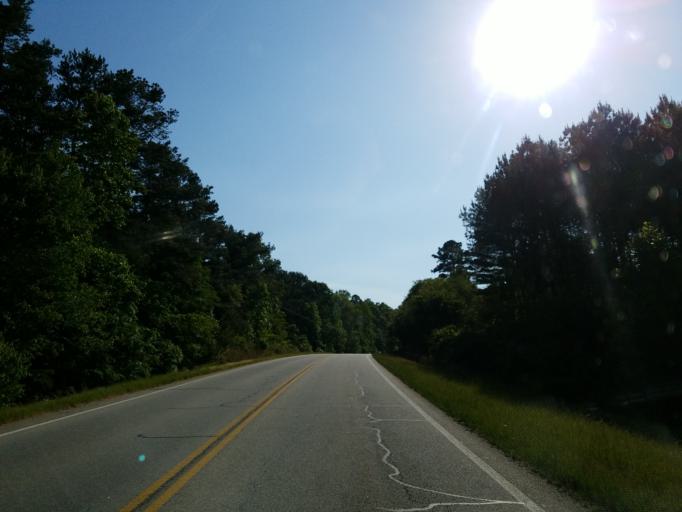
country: US
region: Georgia
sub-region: Paulding County
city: Dallas
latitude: 33.8623
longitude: -84.9084
